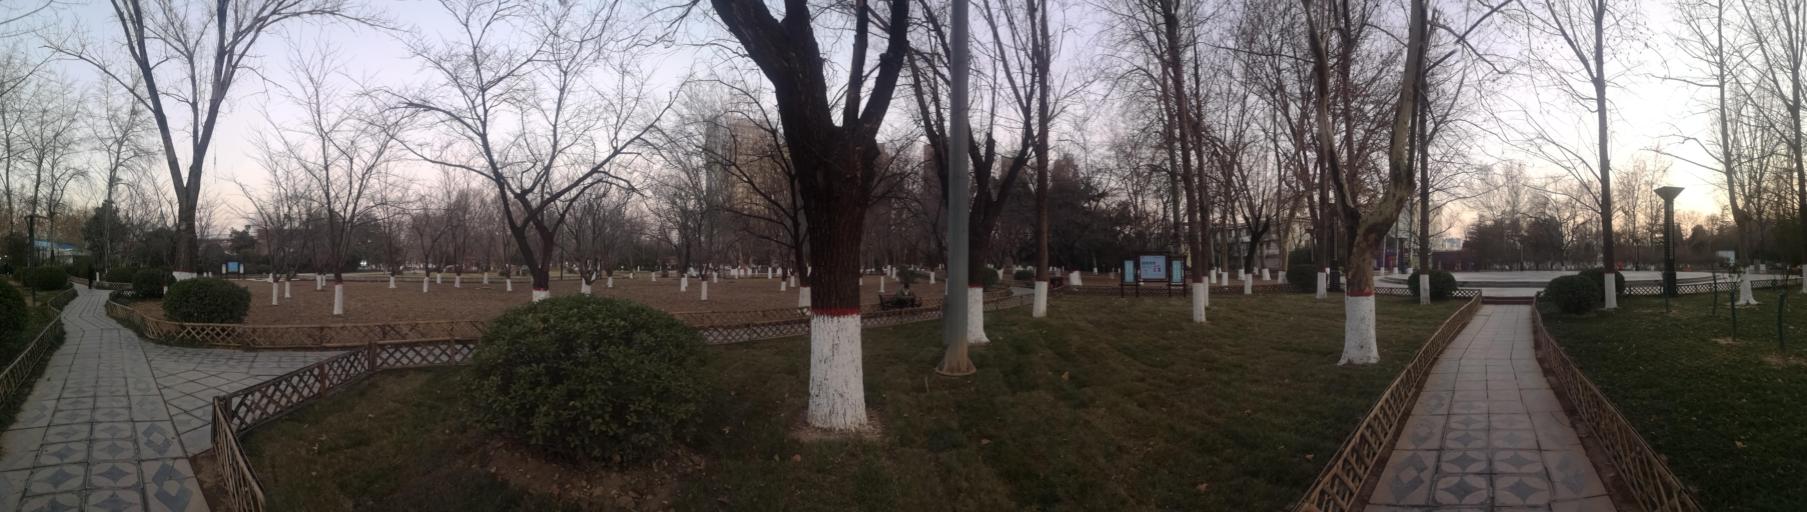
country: CN
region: Henan Sheng
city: Zhongyuanlu
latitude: 35.7739
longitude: 115.0761
